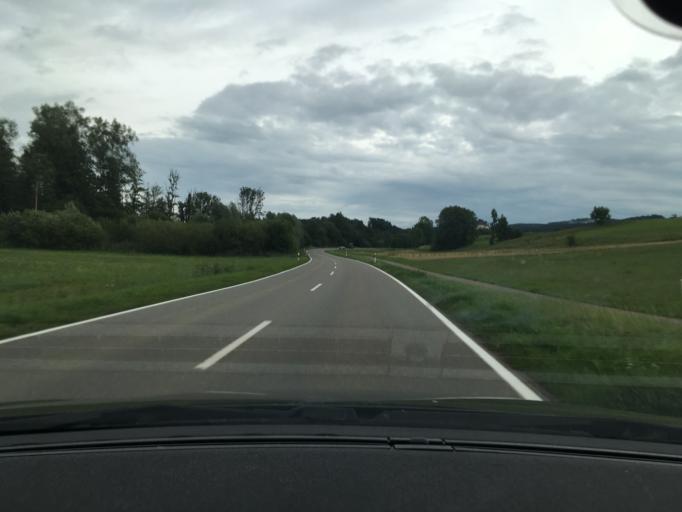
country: DE
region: Baden-Wuerttemberg
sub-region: Tuebingen Region
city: Markdorf
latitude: 47.7784
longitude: 9.3995
